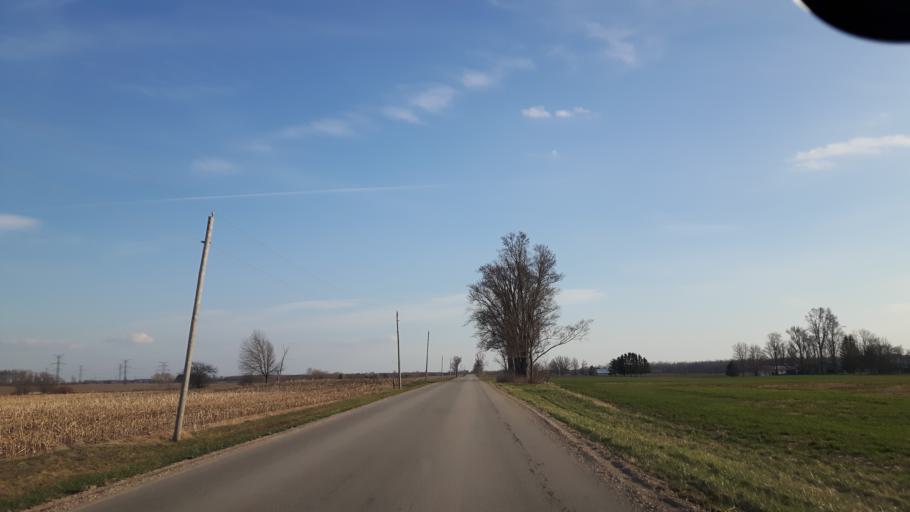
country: CA
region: Ontario
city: Goderich
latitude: 43.6963
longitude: -81.6645
